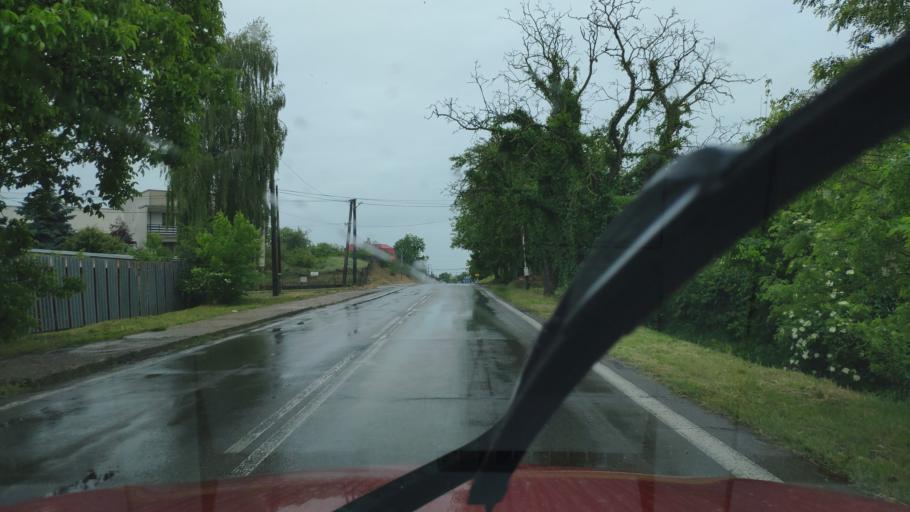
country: HU
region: Borsod-Abauj-Zemplen
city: Ricse
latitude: 48.4311
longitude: 21.9749
